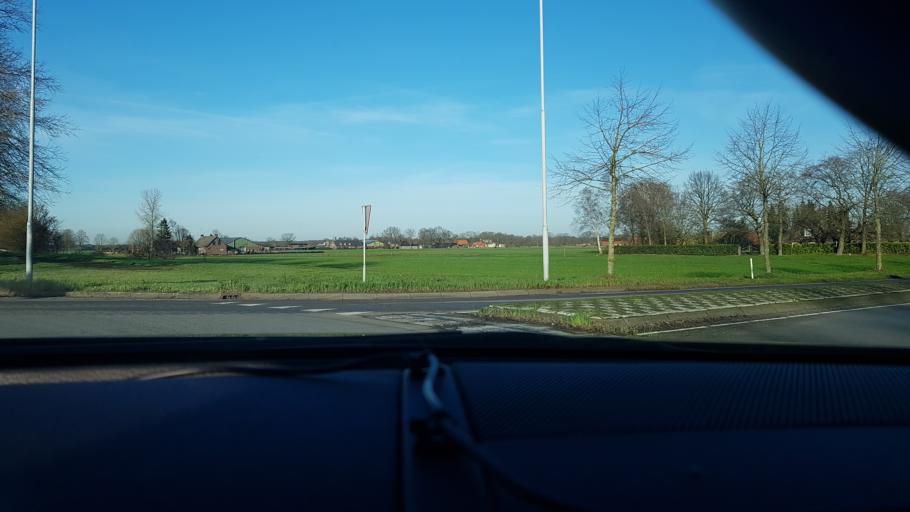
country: NL
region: North Brabant
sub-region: Gemeente Asten
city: Asten
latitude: 51.3989
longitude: 5.7784
